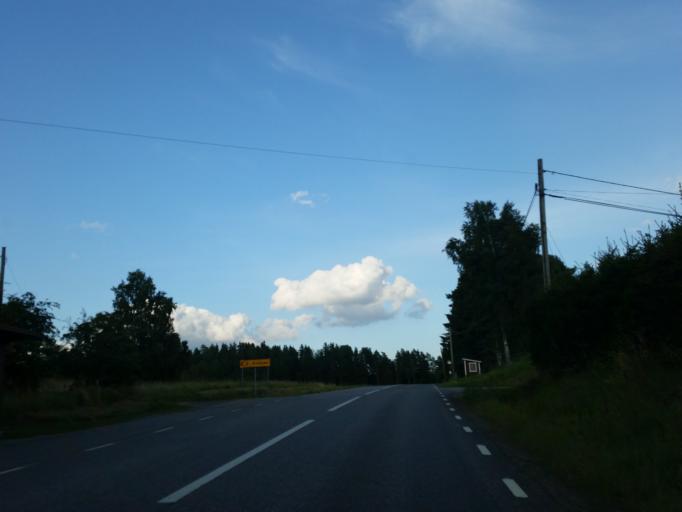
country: SE
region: Stockholm
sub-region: Nykvarns Kommun
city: Nykvarn
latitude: 59.2538
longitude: 17.4558
